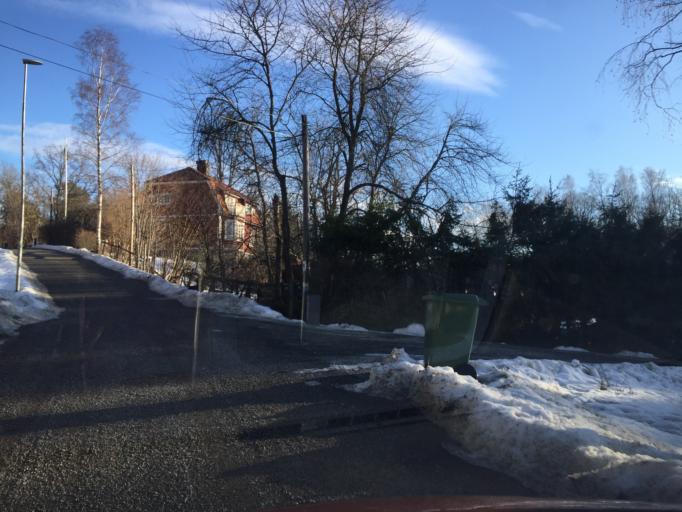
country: SE
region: Stockholm
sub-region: Salems Kommun
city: Ronninge
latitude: 59.1881
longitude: 17.7183
